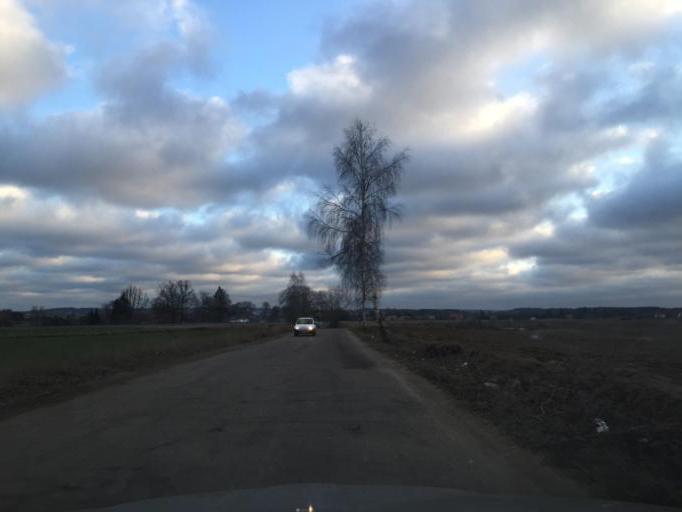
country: PL
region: Pomeranian Voivodeship
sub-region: Powiat kartuski
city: Banino
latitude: 54.3990
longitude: 18.4333
